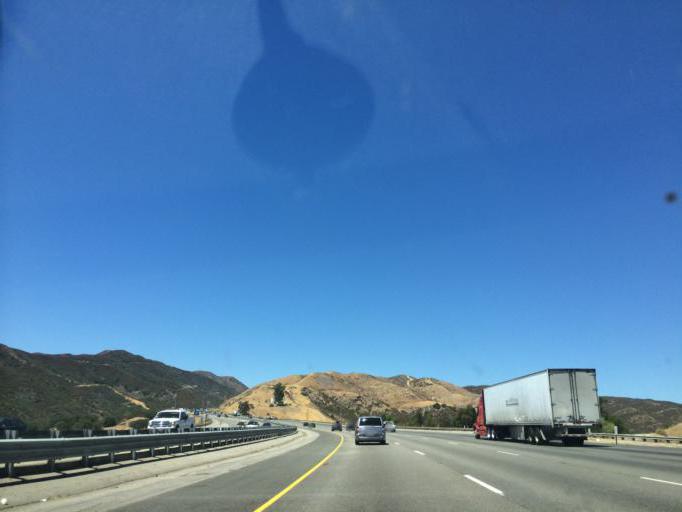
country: US
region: California
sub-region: Los Angeles County
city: Castaic
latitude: 34.5709
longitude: -118.6889
